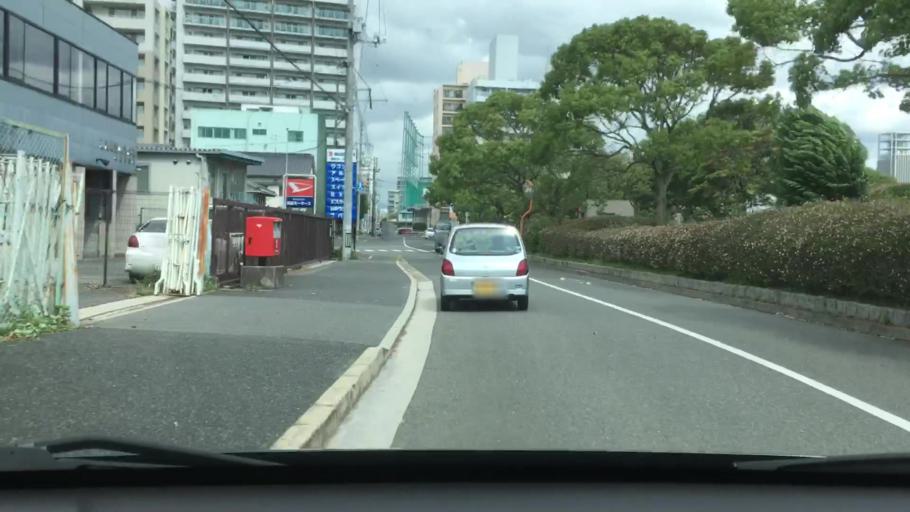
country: JP
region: Hiroshima
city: Hiroshima-shi
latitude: 34.3785
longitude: 132.4430
